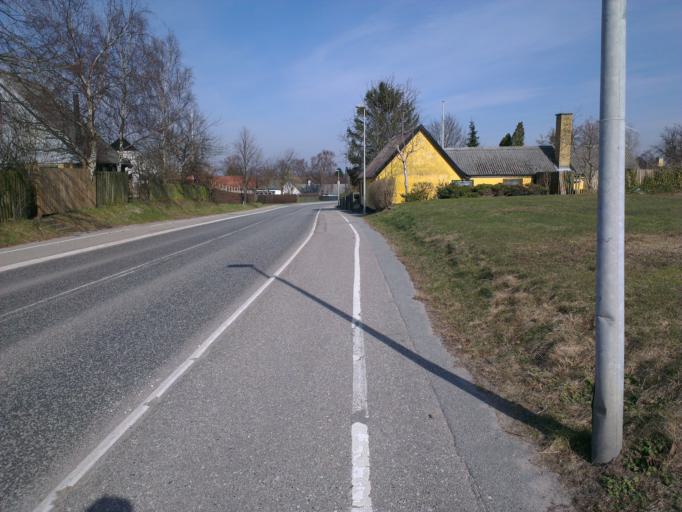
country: DK
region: Capital Region
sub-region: Frederikssund Kommune
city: Jaegerspris
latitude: 55.8233
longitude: 11.9873
